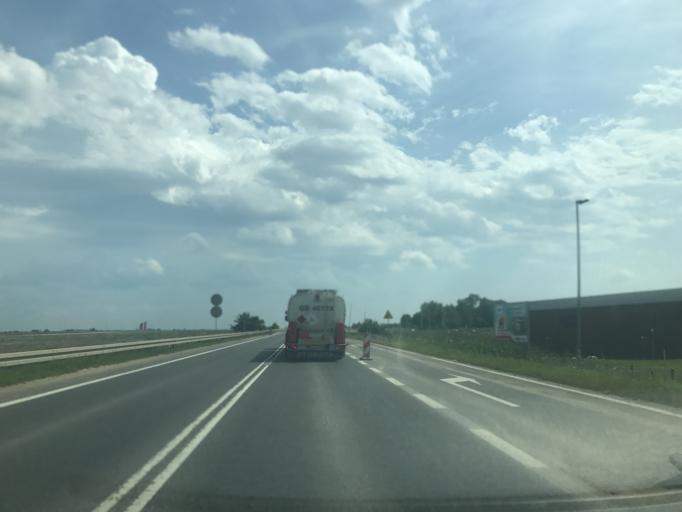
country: PL
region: Warmian-Masurian Voivodeship
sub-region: Powiat ostrodzki
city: Ostroda
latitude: 53.6870
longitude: 19.9957
